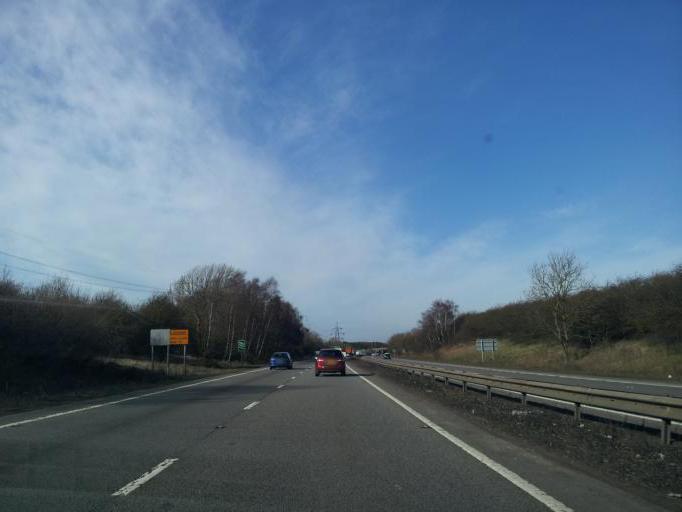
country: GB
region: England
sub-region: Lincolnshire
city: Barrowby
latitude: 52.9125
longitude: -0.6780
